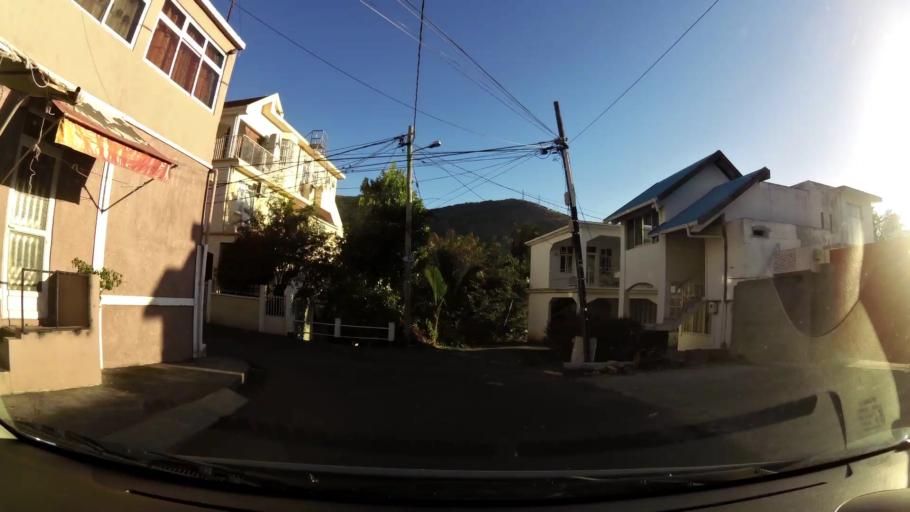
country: MU
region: Port Louis
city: Port Louis
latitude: -20.1741
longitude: 57.5134
